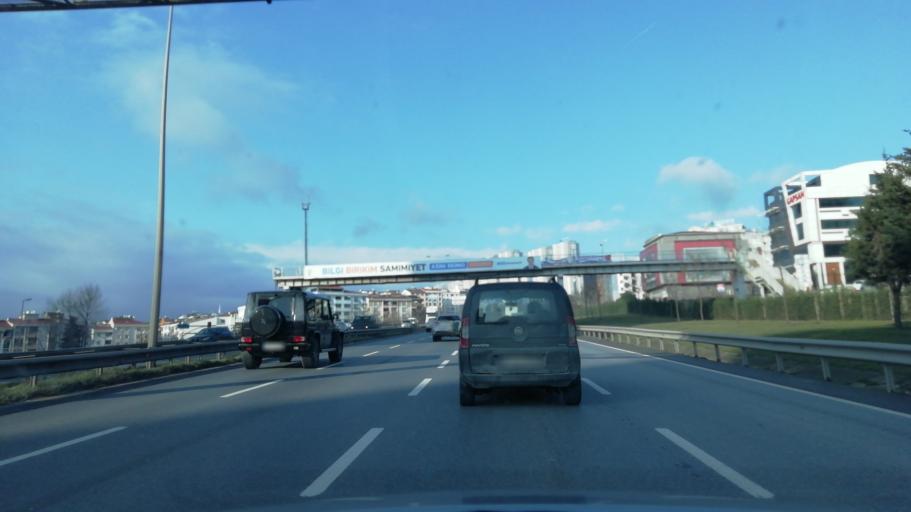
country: TR
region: Istanbul
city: Esenyurt
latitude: 41.0242
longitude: 28.6828
